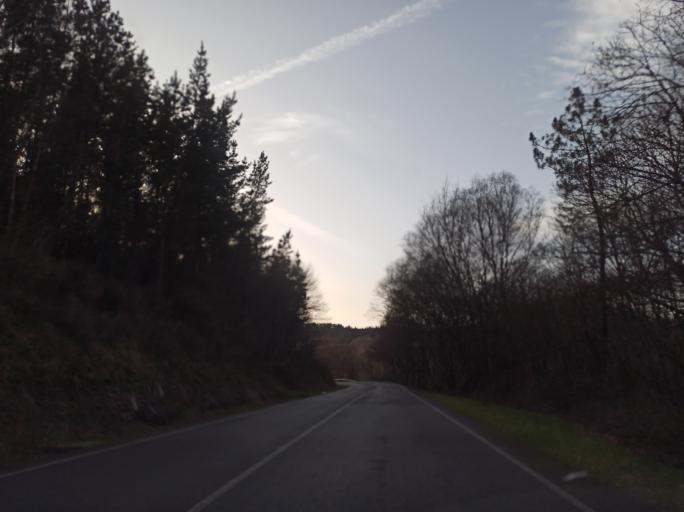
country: ES
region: Galicia
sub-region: Provincia de Lugo
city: Friol
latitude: 43.0253
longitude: -7.8706
